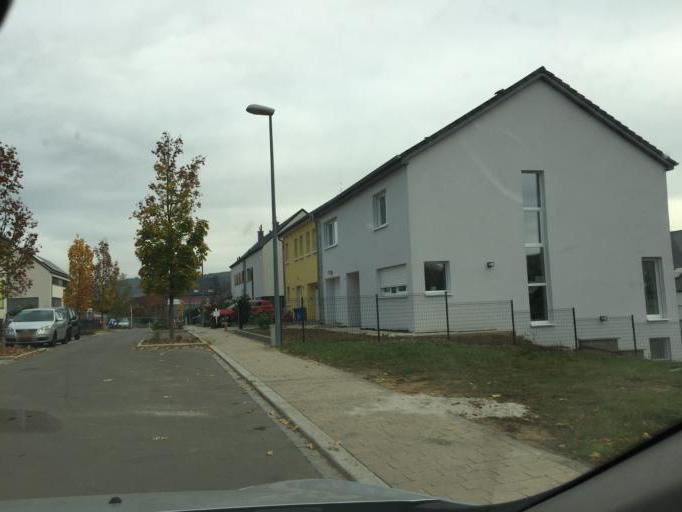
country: LU
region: Luxembourg
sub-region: Canton de Mersch
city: Mersch
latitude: 49.7540
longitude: 6.1046
